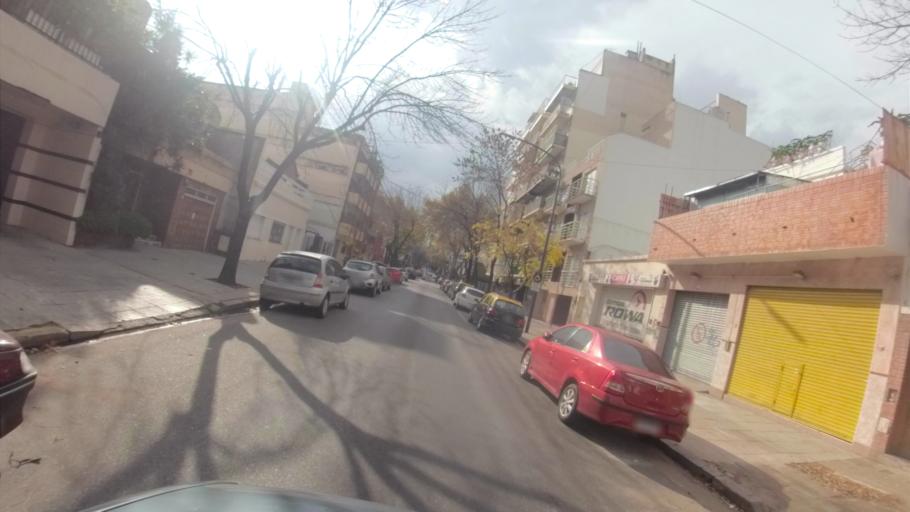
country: AR
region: Buenos Aires F.D.
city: Colegiales
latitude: -34.5811
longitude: -58.4721
